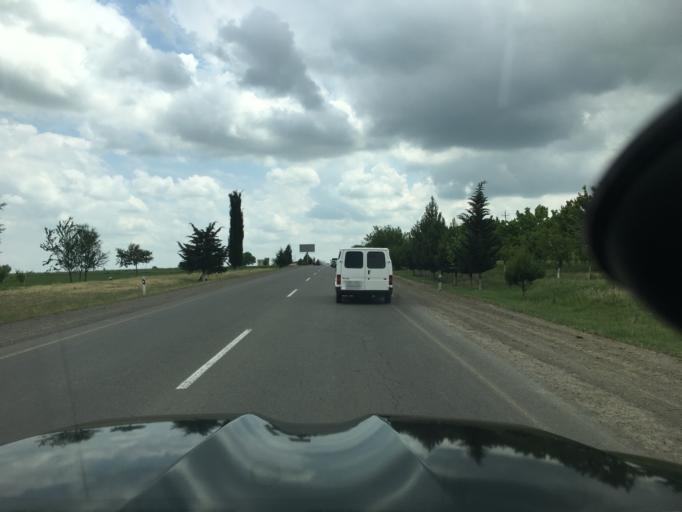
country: AZ
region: Tovuz
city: Tovuz
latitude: 40.9731
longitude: 45.6817
